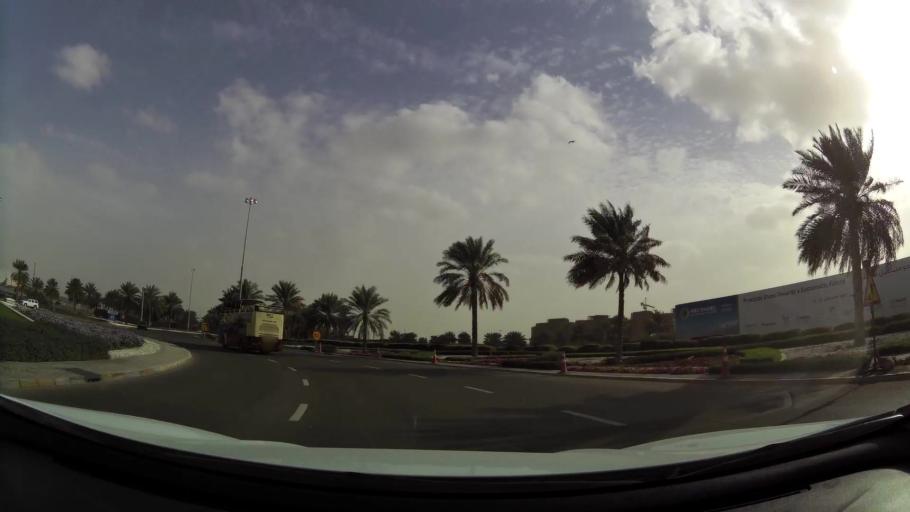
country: AE
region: Abu Dhabi
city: Abu Dhabi
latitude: 24.4398
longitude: 54.6215
